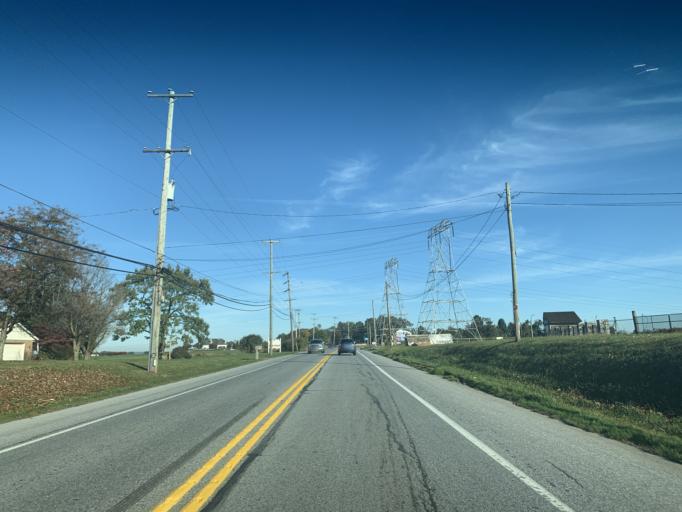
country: US
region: Pennsylvania
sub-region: Chester County
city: Oxford
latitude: 39.8100
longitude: -75.9677
